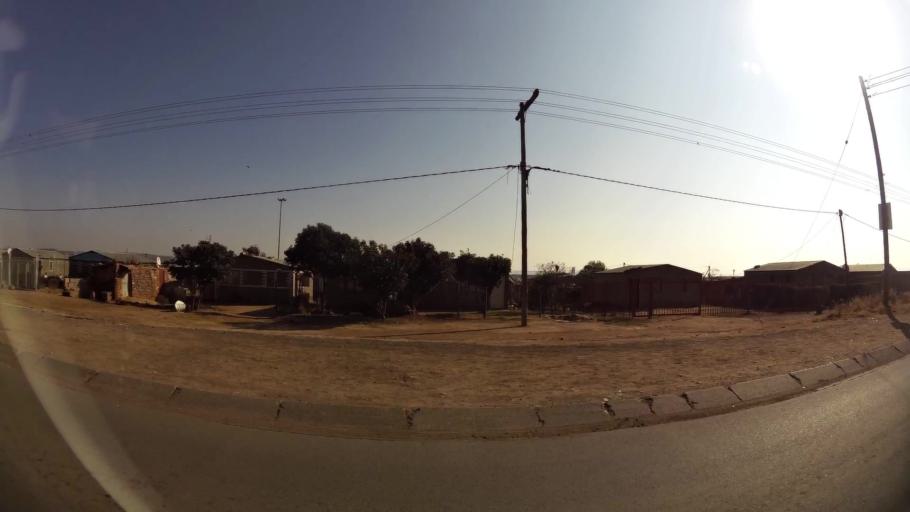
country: ZA
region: Orange Free State
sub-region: Mangaung Metropolitan Municipality
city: Bloemfontein
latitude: -29.1759
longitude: 26.2260
